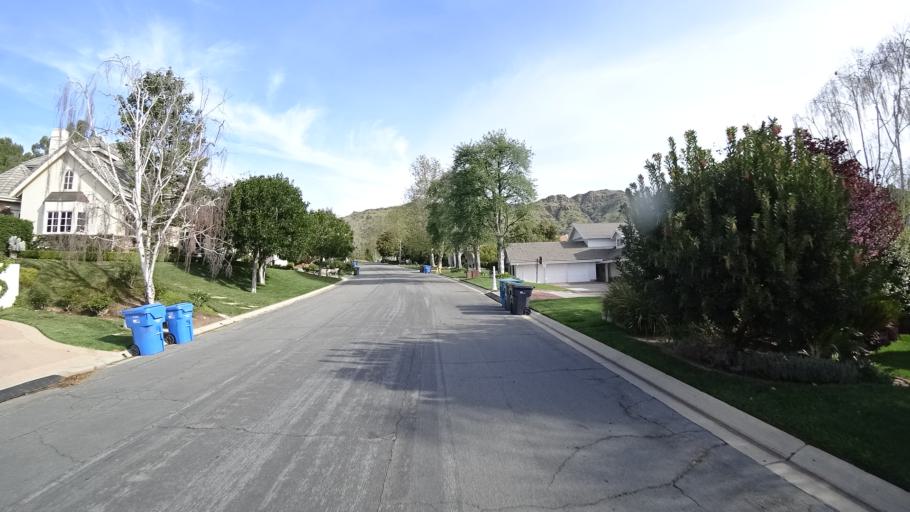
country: US
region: California
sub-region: Ventura County
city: Oak Park
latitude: 34.1905
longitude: -118.7875
